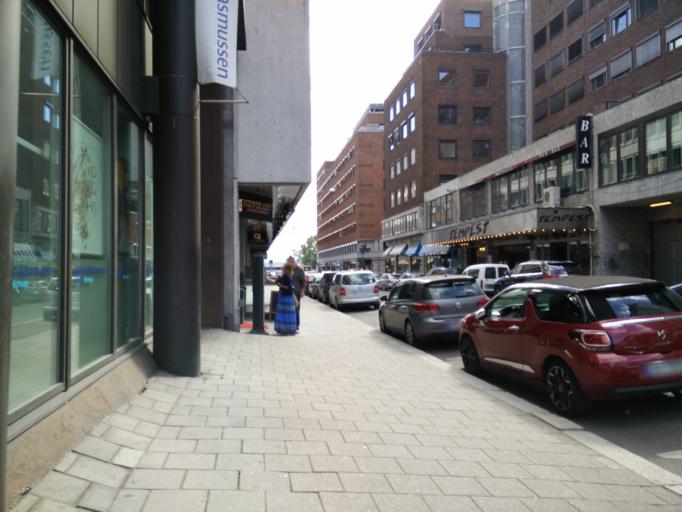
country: NO
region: Oslo
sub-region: Oslo
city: Oslo
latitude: 59.9129
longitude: 10.7355
